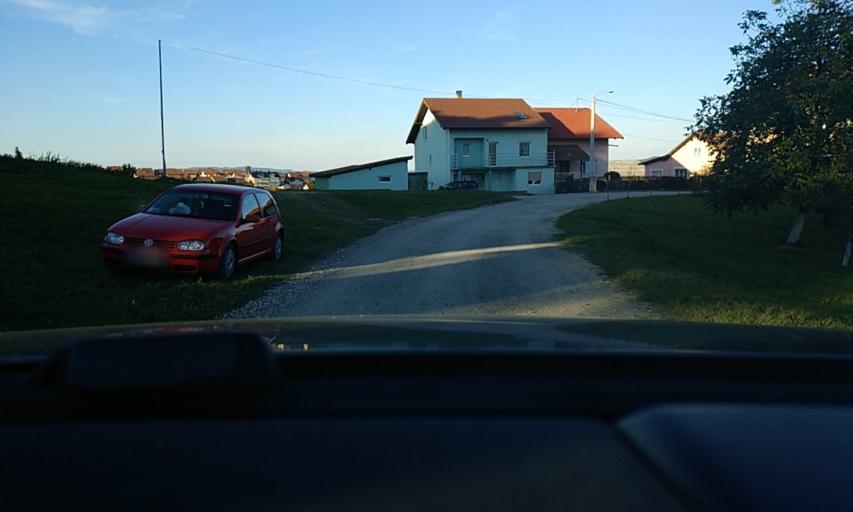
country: BA
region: Republika Srpska
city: Banja Luka
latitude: 44.7850
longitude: 17.1809
